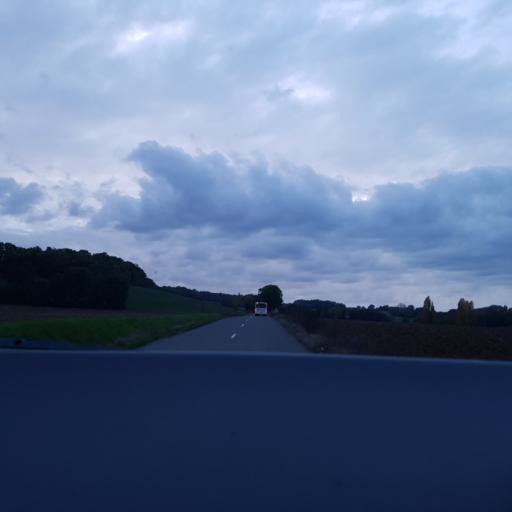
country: FR
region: Midi-Pyrenees
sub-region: Departement du Gers
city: Condom
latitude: 43.9496
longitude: 0.2925
